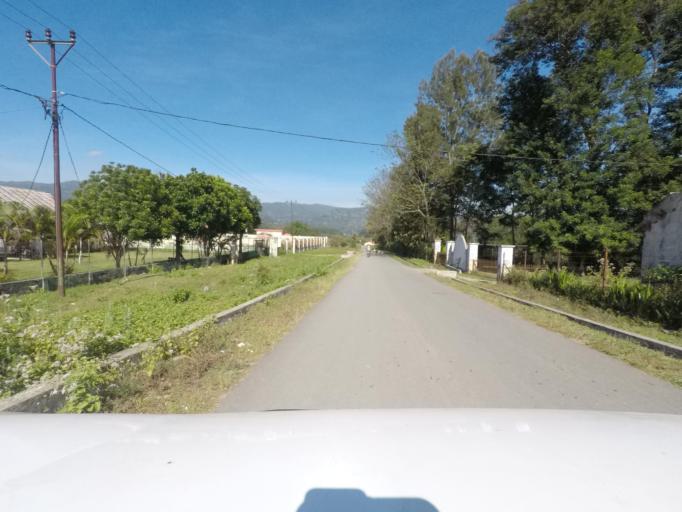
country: TL
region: Ermera
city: Gleno
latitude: -8.7130
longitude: 125.4527
